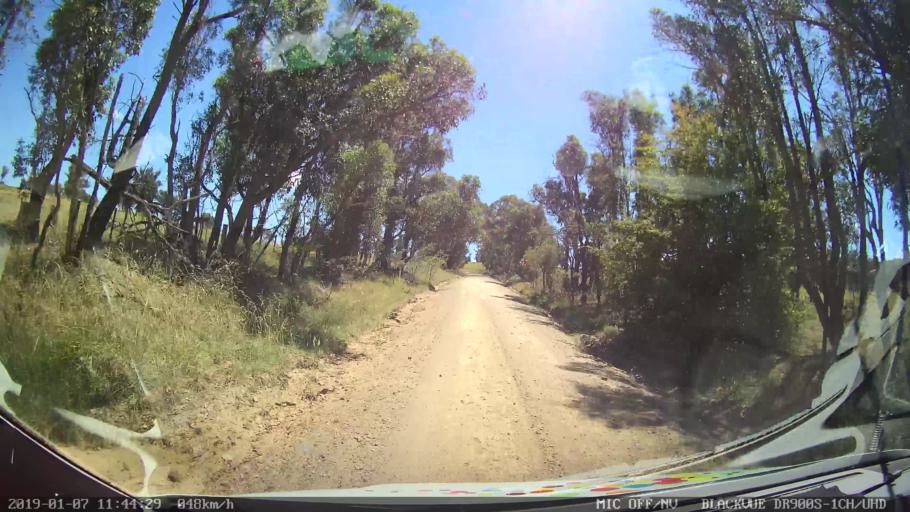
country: AU
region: New South Wales
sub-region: Guyra
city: Guyra
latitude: -30.3523
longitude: 151.6064
